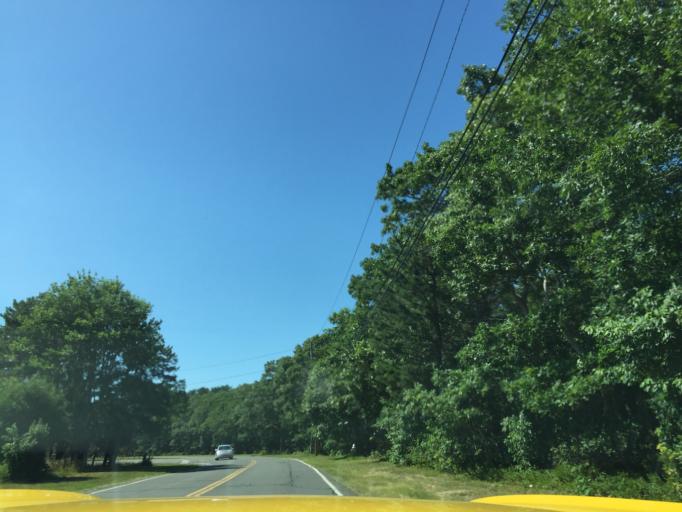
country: US
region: New York
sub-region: Suffolk County
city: Northwest Harbor
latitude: 40.9624
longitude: -72.2472
